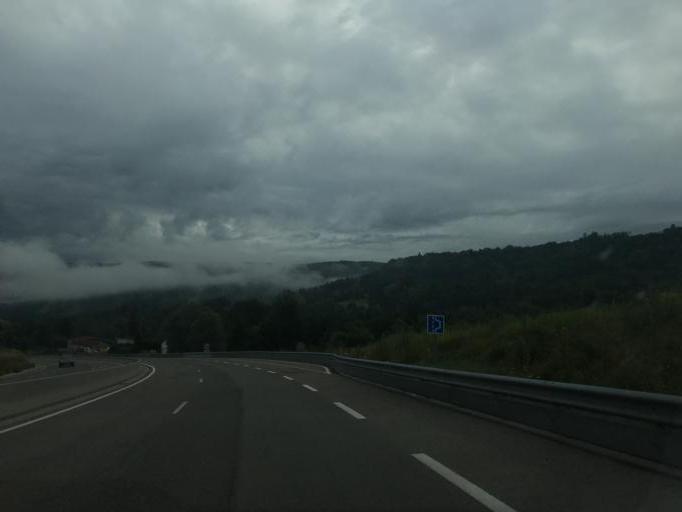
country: FR
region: Rhone-Alpes
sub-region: Departement de l'Ain
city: Dortan
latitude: 46.2999
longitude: 5.6557
